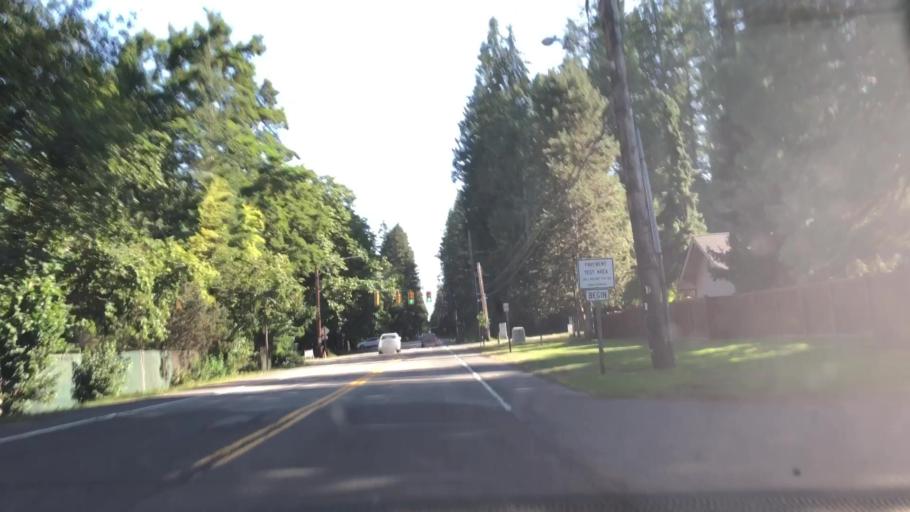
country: US
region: Washington
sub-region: King County
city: Cottage Lake
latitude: 47.7408
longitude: -122.0779
